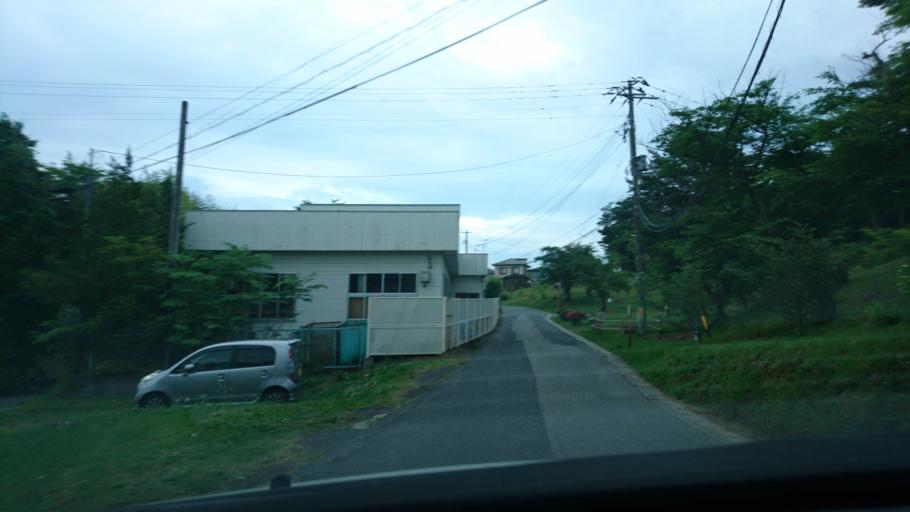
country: JP
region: Iwate
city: Ichinoseki
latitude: 38.9103
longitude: 141.1683
